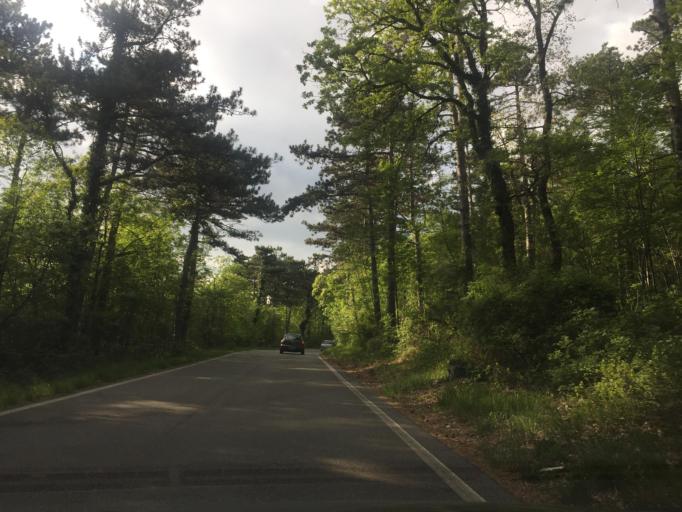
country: IT
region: Friuli Venezia Giulia
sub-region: Provincia di Trieste
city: Dolina
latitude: 45.6303
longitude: 13.8778
